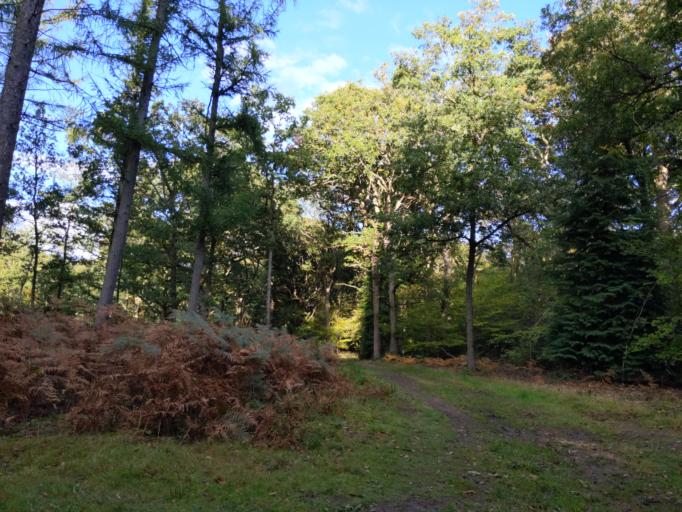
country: GB
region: England
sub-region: Oxfordshire
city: Boars Hill
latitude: 51.7165
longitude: -1.2619
